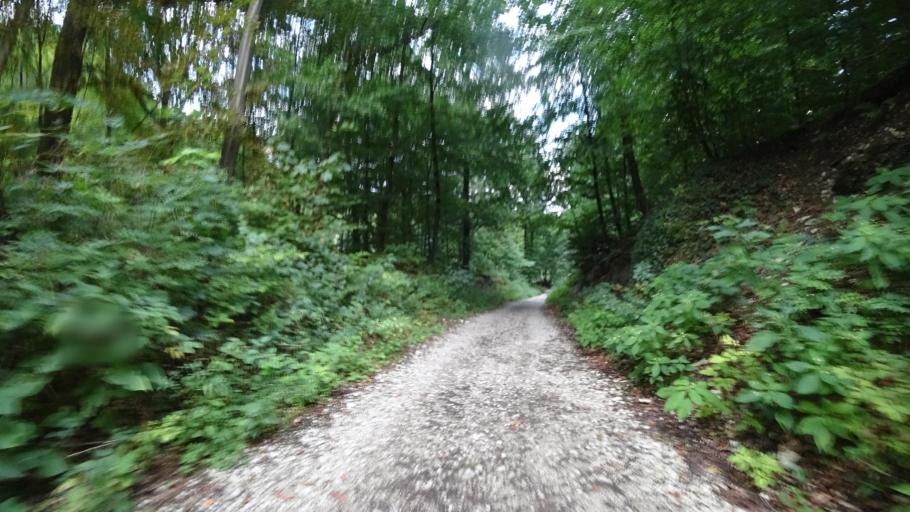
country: DE
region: North Rhine-Westphalia
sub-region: Regierungsbezirk Detmold
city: Bielefeld
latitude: 52.0109
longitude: 8.4950
